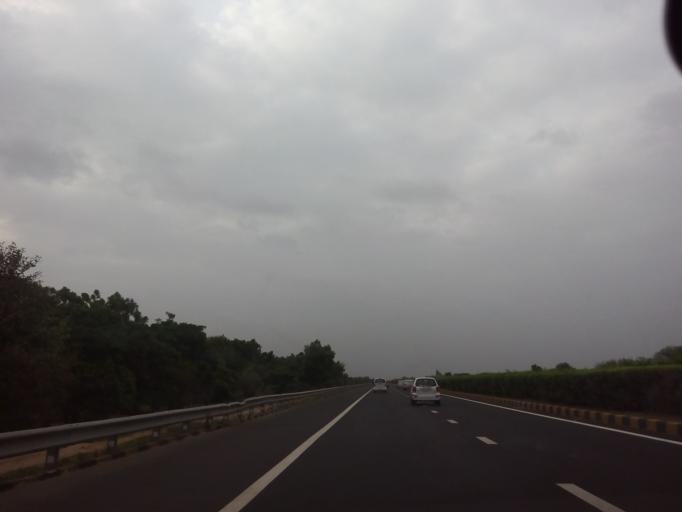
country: IN
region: Gujarat
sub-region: Kheda
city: Chaklasi
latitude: 22.6429
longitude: 72.9353
